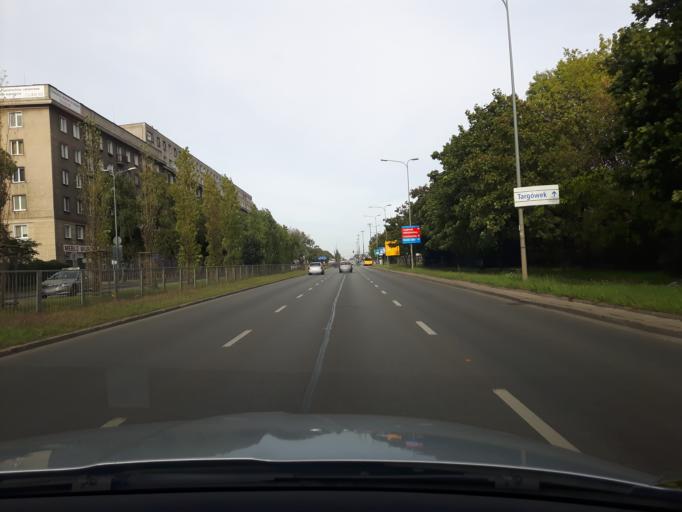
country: PL
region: Masovian Voivodeship
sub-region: Warszawa
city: Praga Polnoc
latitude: 52.2586
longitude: 21.0440
